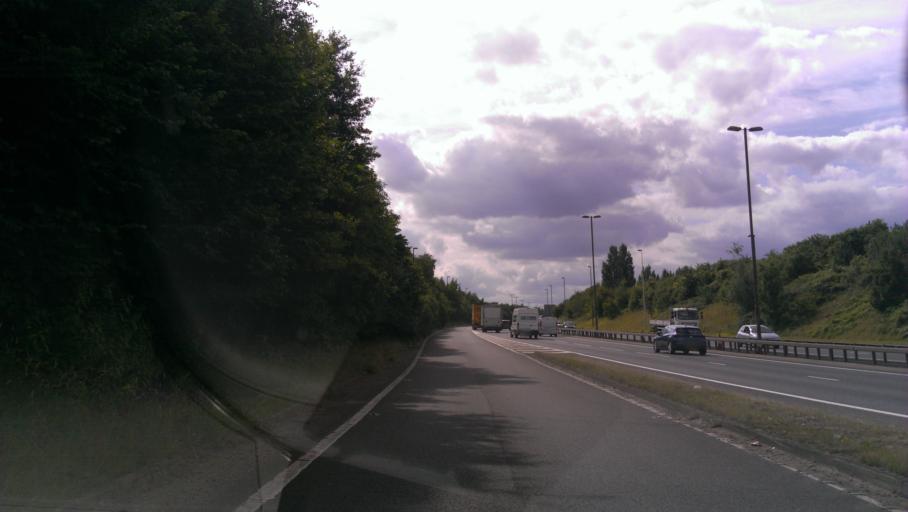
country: GB
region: England
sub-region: Kent
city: Strood
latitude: 51.4103
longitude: 0.4940
